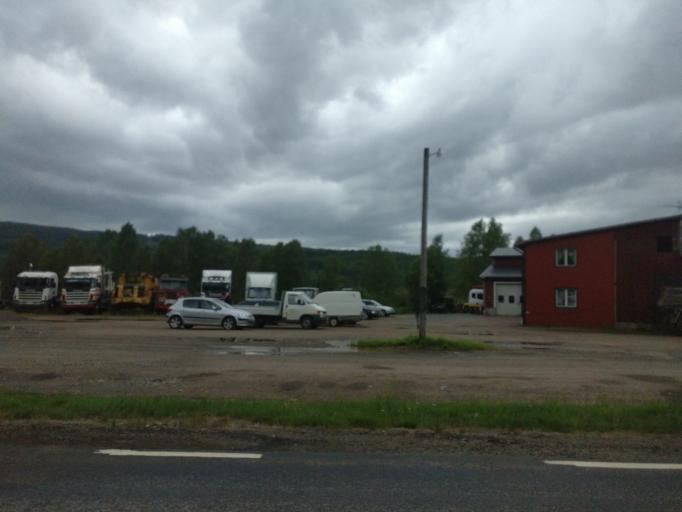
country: SE
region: Vaermland
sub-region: Torsby Kommun
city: Torsby
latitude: 60.6269
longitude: 13.0267
